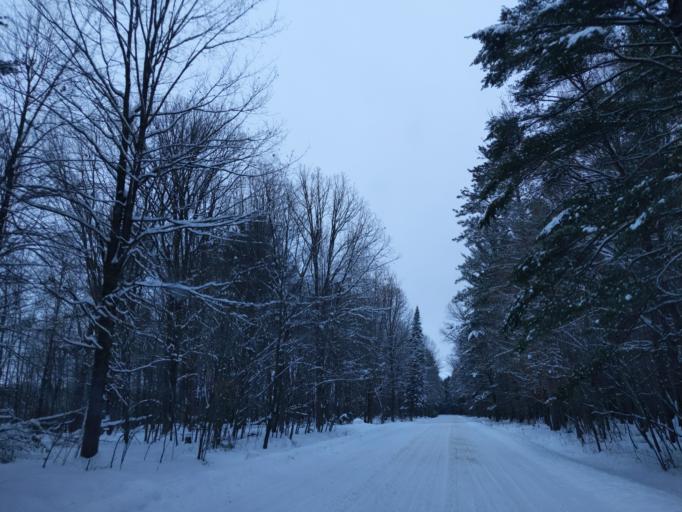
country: US
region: Wisconsin
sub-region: Marathon County
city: Marathon
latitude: 44.7637
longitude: -89.8696
